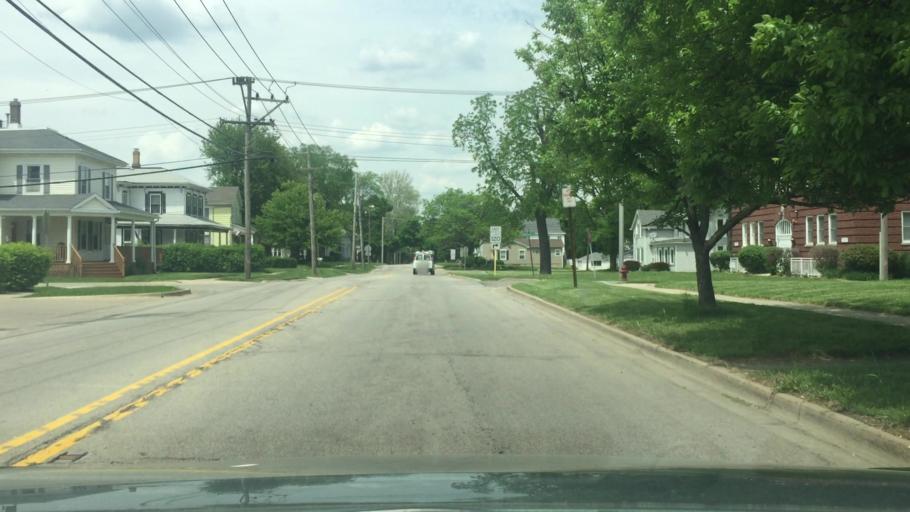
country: US
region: Illinois
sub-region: McHenry County
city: Woodstock
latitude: 42.3173
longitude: -88.4449
